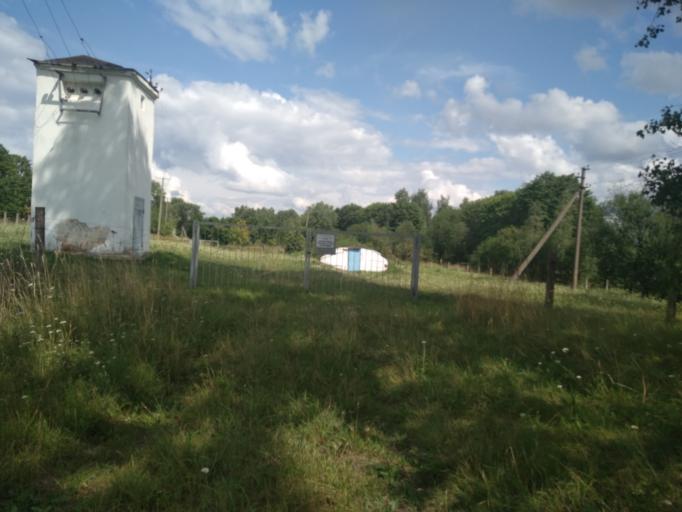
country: BY
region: Minsk
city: Minsk
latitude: 53.9440
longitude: 27.5656
